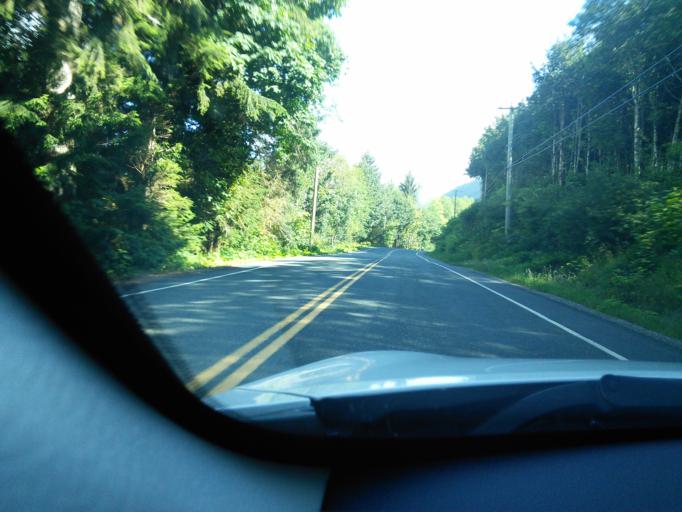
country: CA
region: British Columbia
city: Campbell River
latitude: 50.3434
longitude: -125.9069
